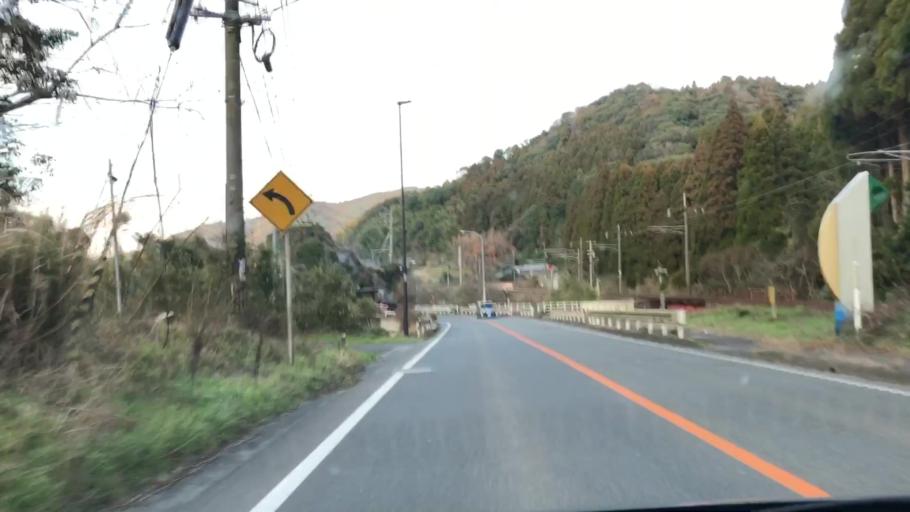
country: JP
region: Kumamoto
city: Minamata
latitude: 32.2190
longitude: 130.4381
